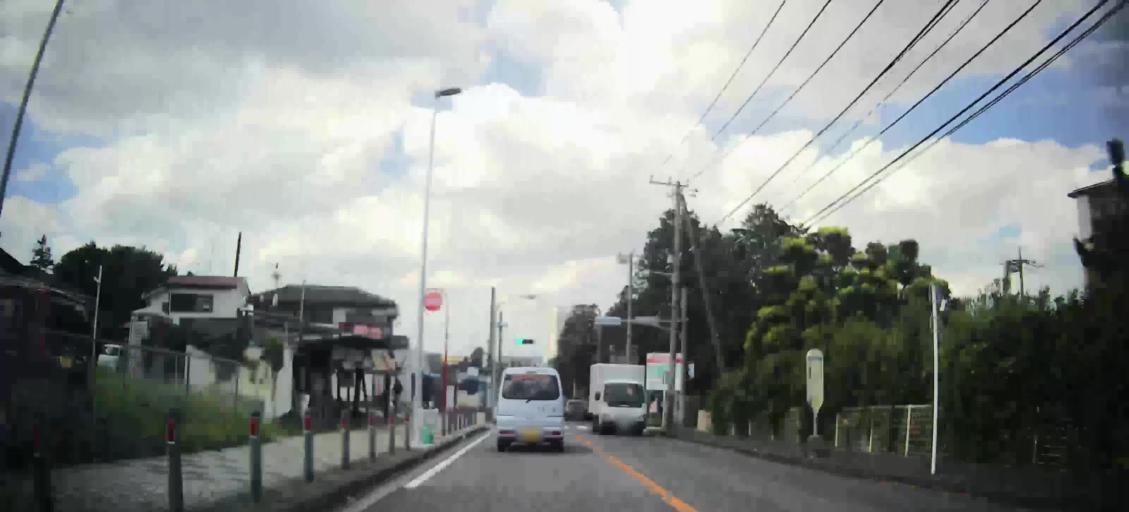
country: JP
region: Kanagawa
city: Yokohama
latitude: 35.4690
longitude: 139.5581
